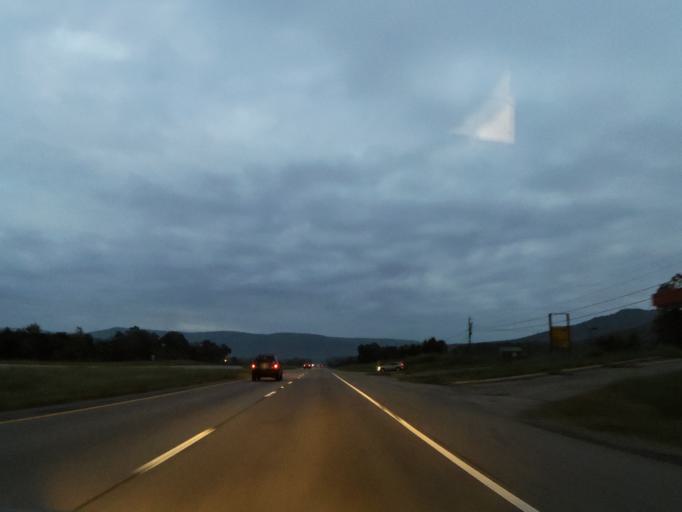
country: US
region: Alabama
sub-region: Madison County
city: Owens Cross Roads
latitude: 34.6920
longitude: -86.3555
